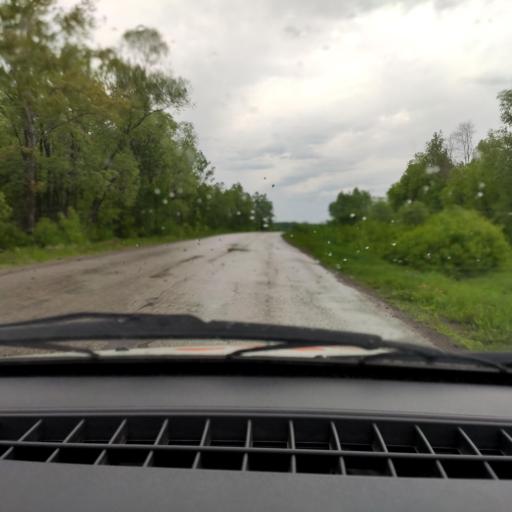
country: RU
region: Bashkortostan
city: Urman
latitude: 54.8629
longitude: 56.8394
